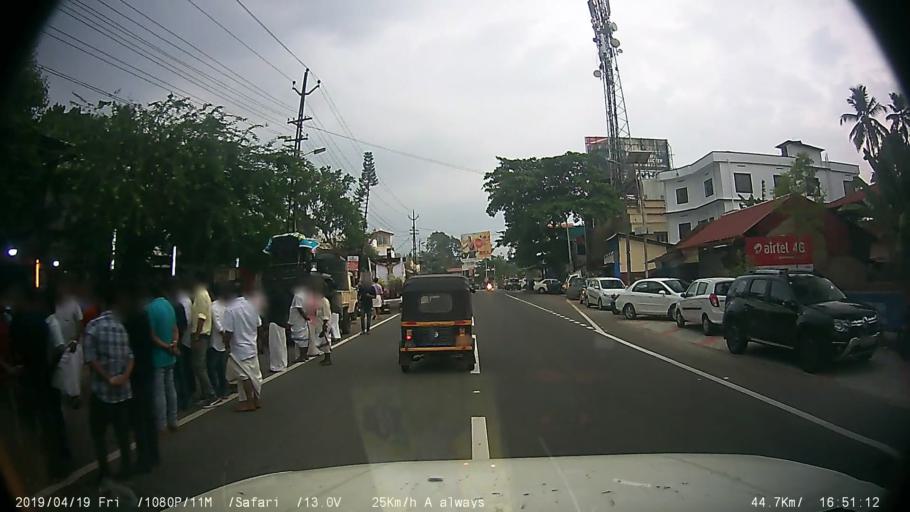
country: IN
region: Kerala
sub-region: Kottayam
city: Changanacheri
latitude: 9.4583
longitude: 76.5335
